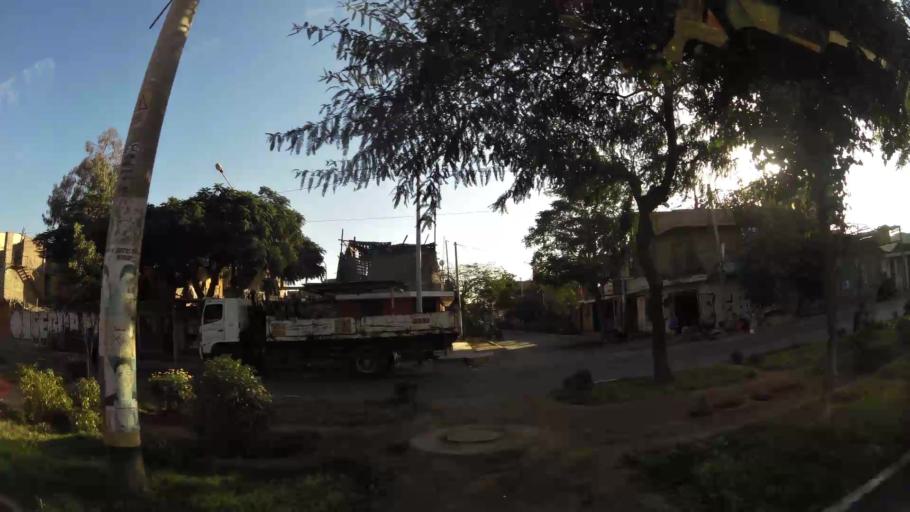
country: PE
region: Ica
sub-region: Provincia de Ica
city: Ica
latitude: -14.0628
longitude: -75.7210
